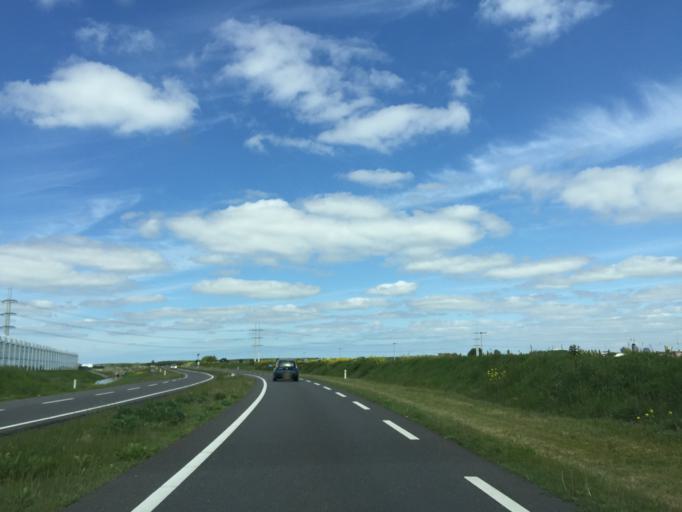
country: NL
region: South Holland
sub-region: Gemeente Lansingerland
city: Berkel en Rodenrijs
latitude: 52.0227
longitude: 4.4760
